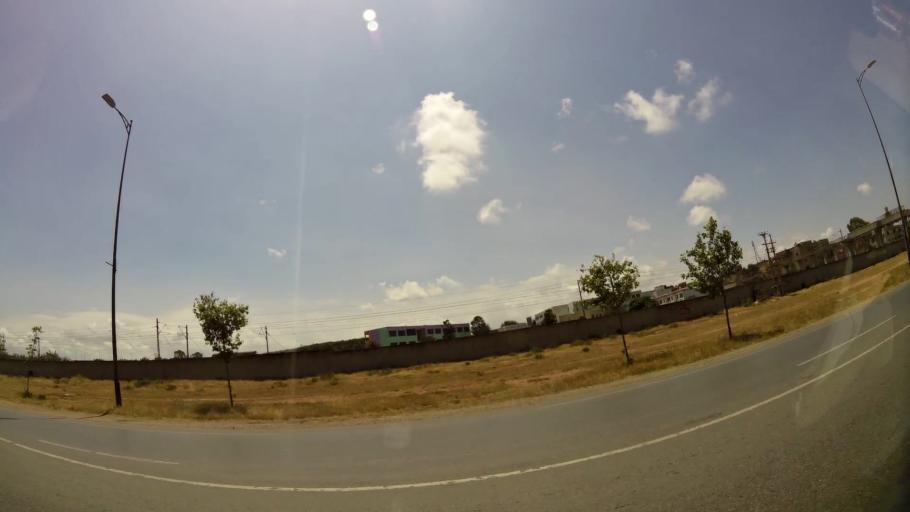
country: MA
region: Rabat-Sale-Zemmour-Zaer
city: Sale
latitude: 34.0738
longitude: -6.7852
